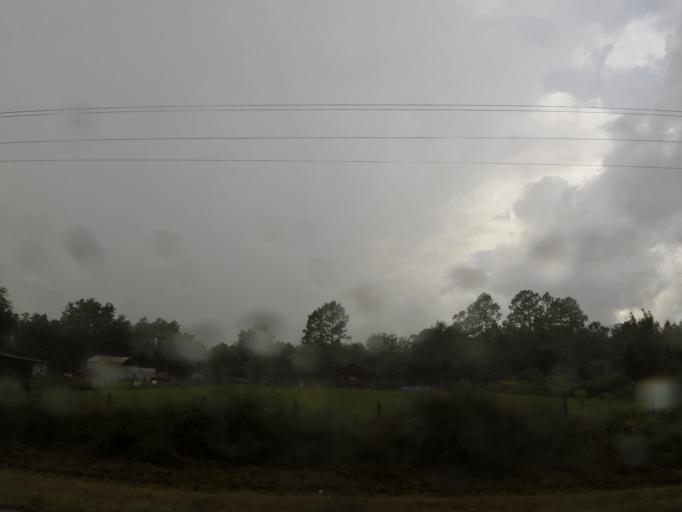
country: US
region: Florida
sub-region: Nassau County
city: Hilliard
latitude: 30.5374
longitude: -82.0395
